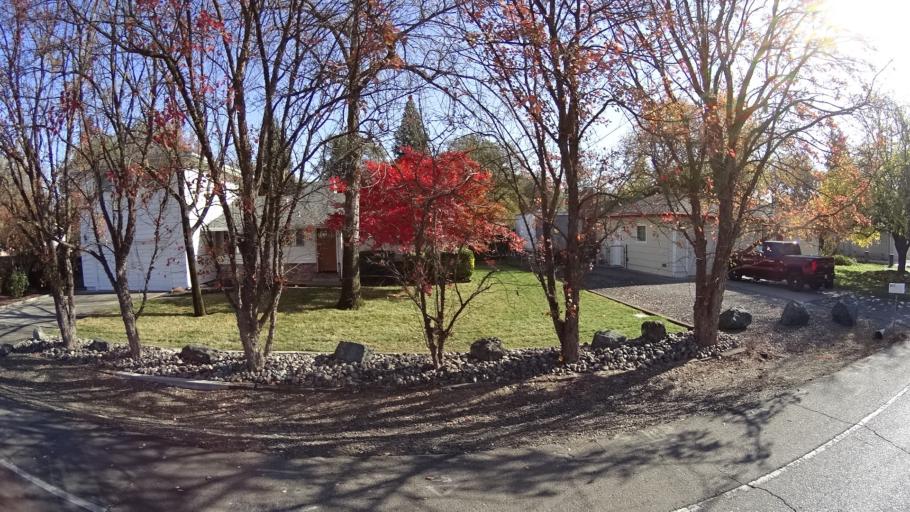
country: US
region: California
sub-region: Sacramento County
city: Citrus Heights
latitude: 38.6894
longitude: -121.2835
